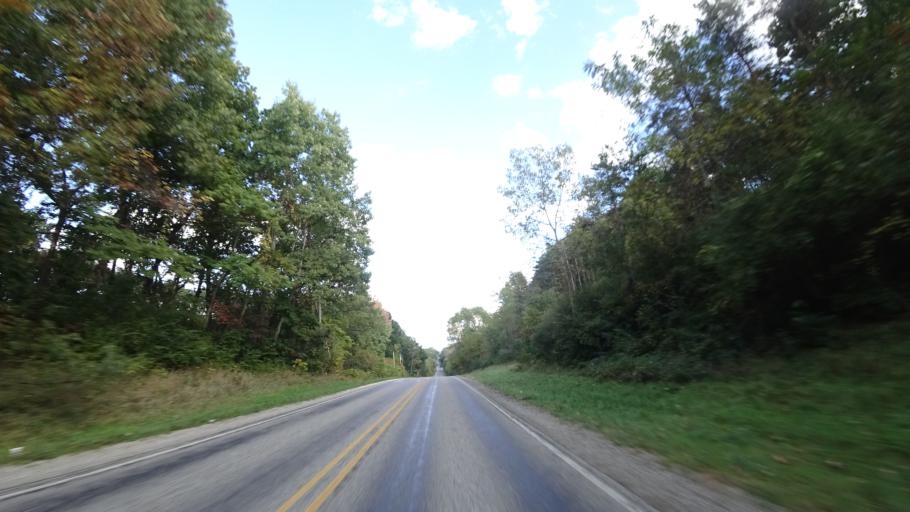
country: US
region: Michigan
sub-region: Saint Joseph County
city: Sturgis
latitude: 41.8538
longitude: -85.4486
